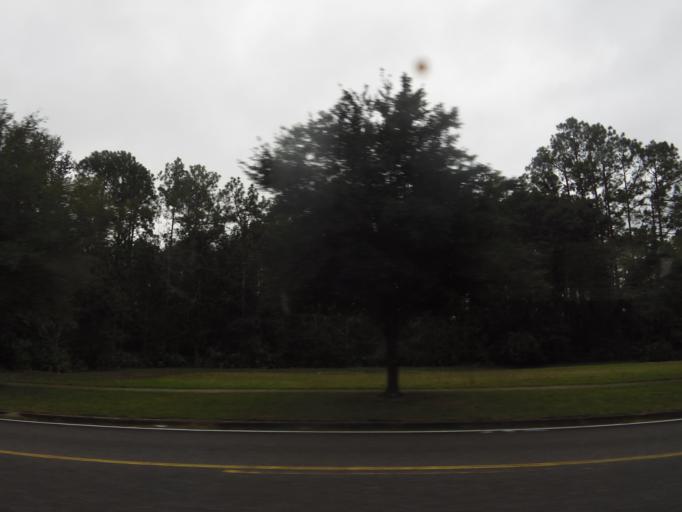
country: US
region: Florida
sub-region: Duval County
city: Baldwin
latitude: 30.2337
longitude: -81.8848
